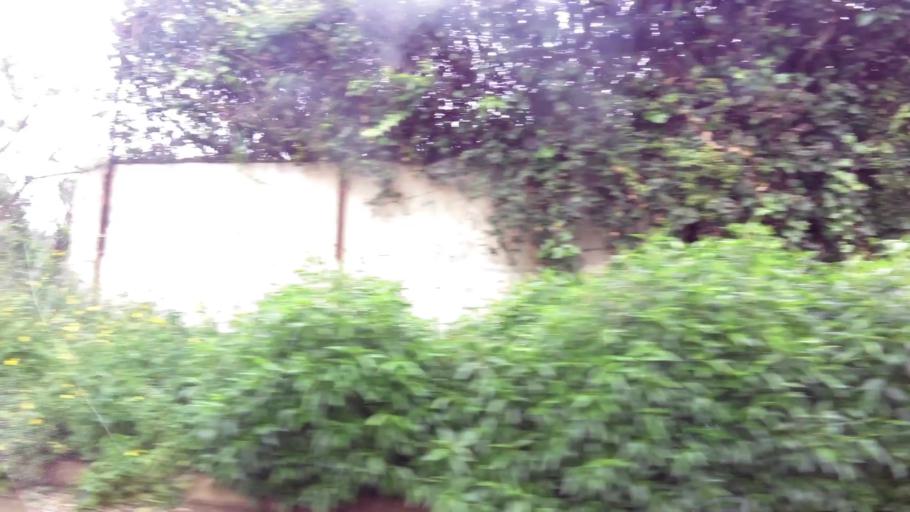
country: MA
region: Grand Casablanca
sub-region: Casablanca
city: Casablanca
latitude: 33.5401
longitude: -7.6501
